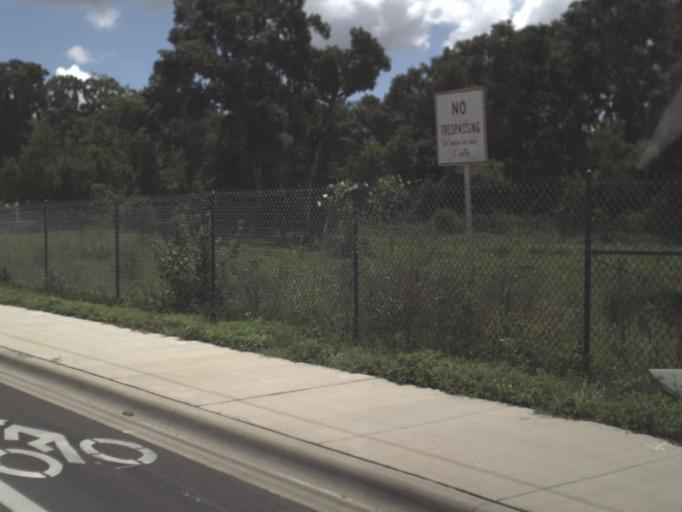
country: US
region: Florida
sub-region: Hillsborough County
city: Mango
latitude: 27.9814
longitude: -82.2950
